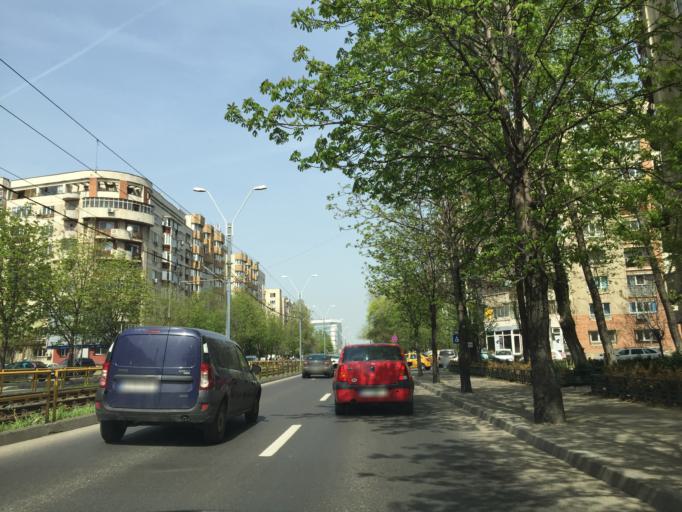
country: RO
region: Ilfov
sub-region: Comuna Chiajna
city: Rosu
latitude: 44.4384
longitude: 26.0354
